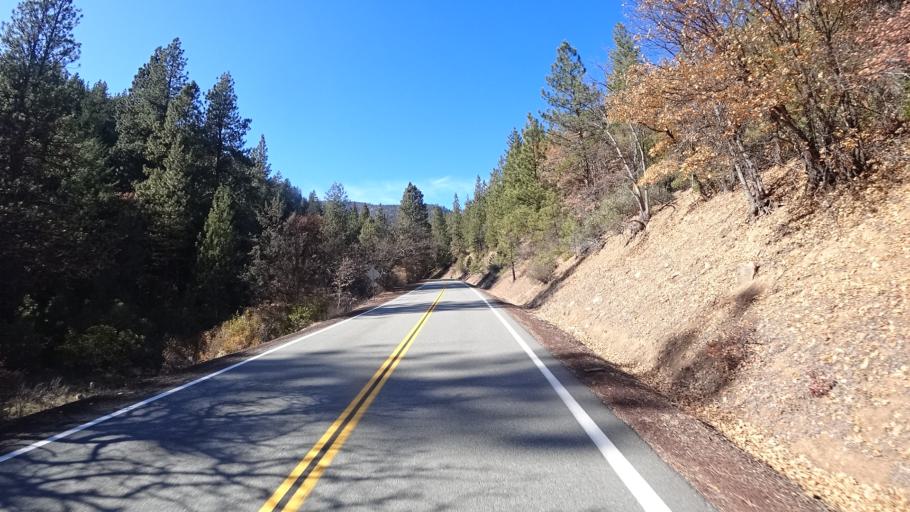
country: US
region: California
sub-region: Siskiyou County
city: Weed
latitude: 41.4561
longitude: -122.6367
